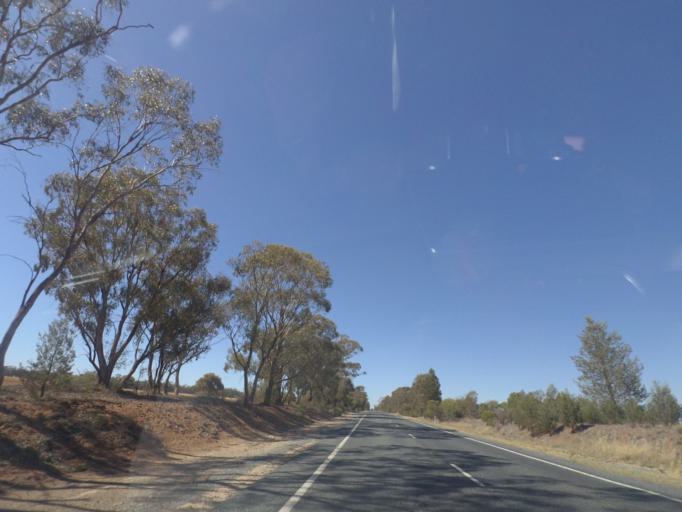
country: AU
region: New South Wales
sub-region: Bland
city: West Wyalong
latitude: -34.1575
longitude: 147.1173
